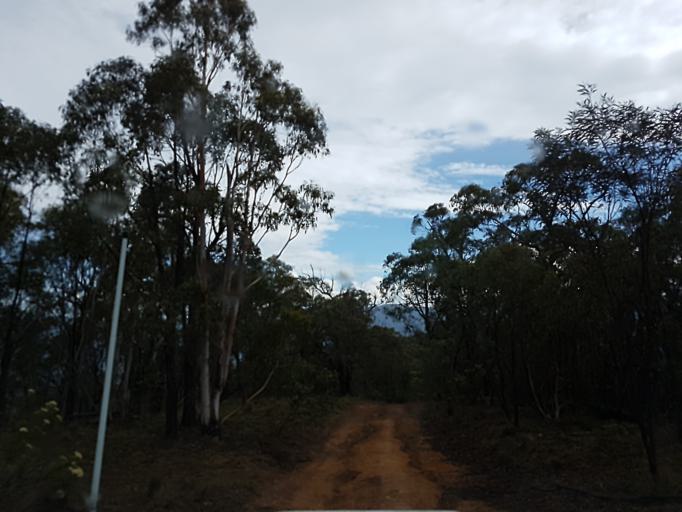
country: AU
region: New South Wales
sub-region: Snowy River
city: Jindabyne
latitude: -36.9081
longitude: 148.3395
